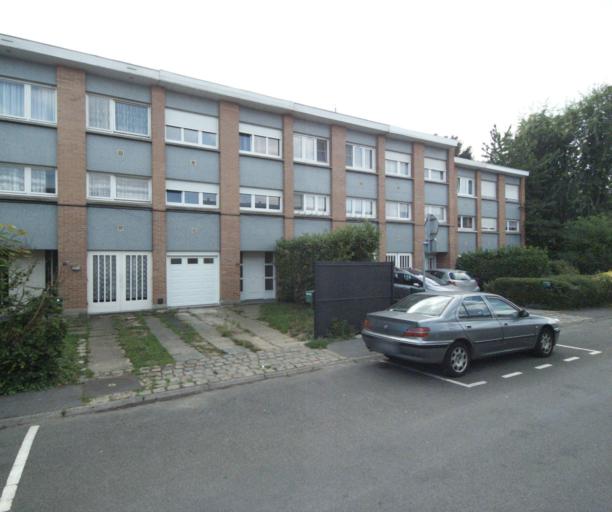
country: FR
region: Nord-Pas-de-Calais
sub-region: Departement du Nord
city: Mons-en-Baroeul
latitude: 50.6368
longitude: 3.1141
